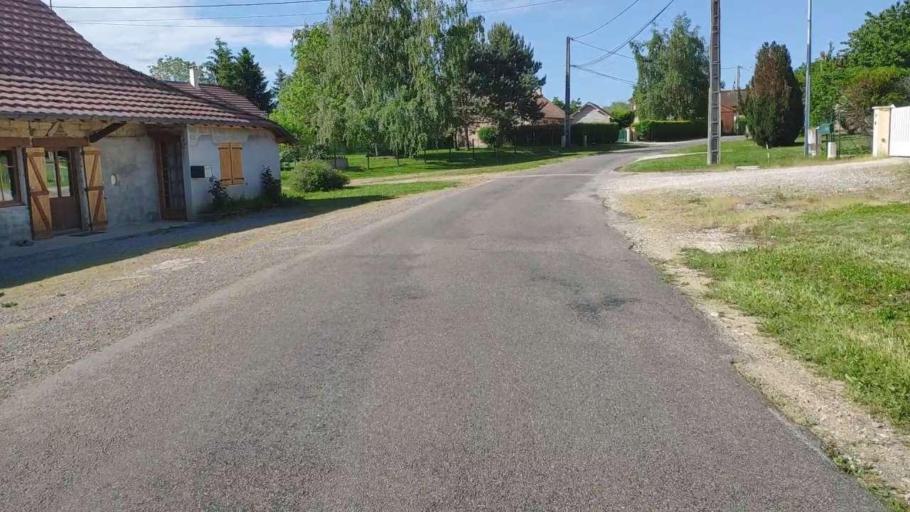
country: FR
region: Franche-Comte
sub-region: Departement du Jura
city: Bletterans
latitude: 46.7116
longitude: 5.4700
